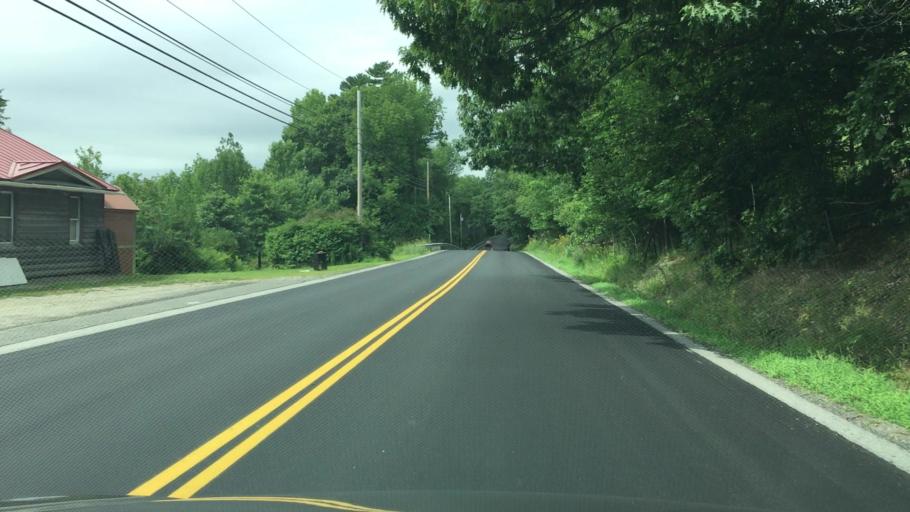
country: US
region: Maine
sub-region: Waldo County
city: Winterport
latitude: 44.6104
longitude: -68.8224
